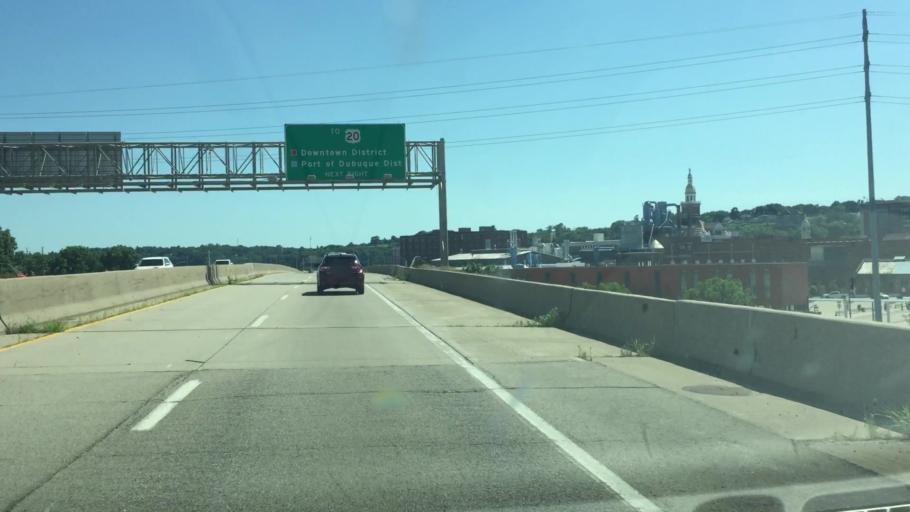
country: US
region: Iowa
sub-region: Dubuque County
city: Dubuque
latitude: 42.5053
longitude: -90.6604
